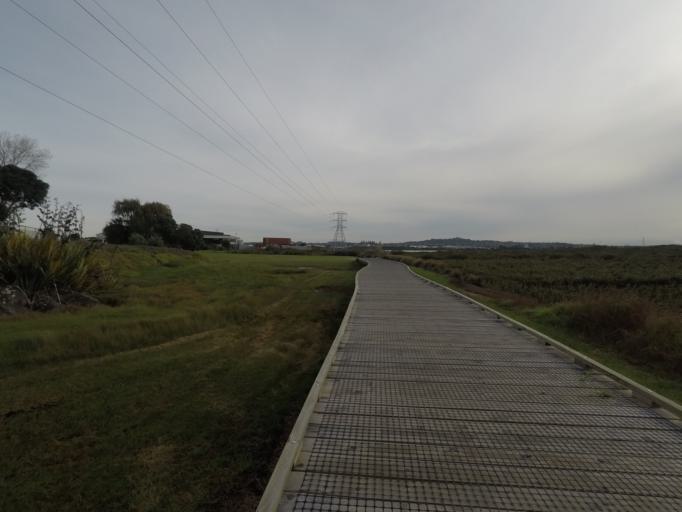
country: NZ
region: Auckland
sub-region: Auckland
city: Mangere
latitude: -36.9433
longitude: 174.7981
